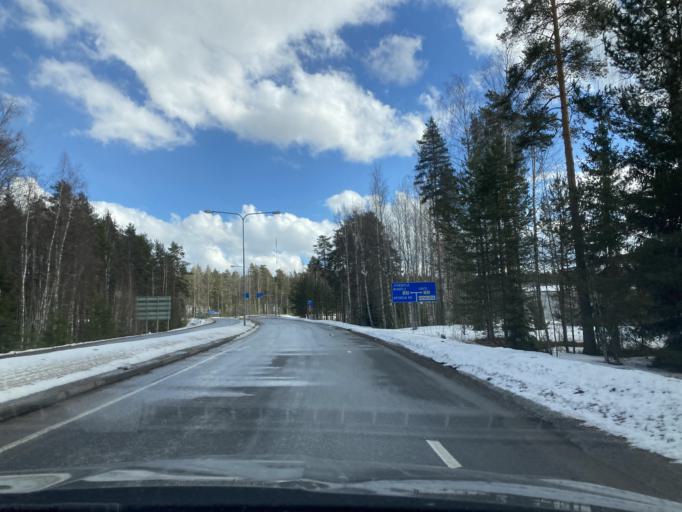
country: FI
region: Paijanne Tavastia
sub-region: Lahti
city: Heinola
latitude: 61.2321
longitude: 26.0481
